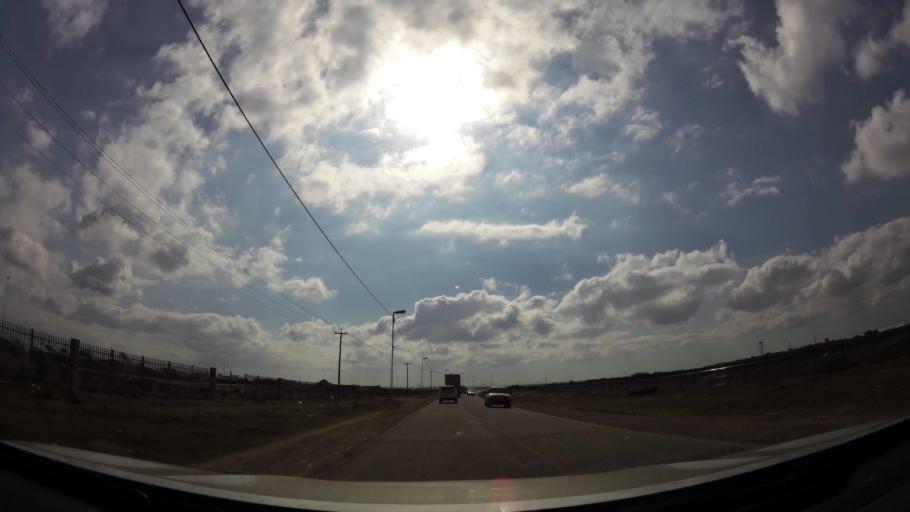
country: ZA
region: Eastern Cape
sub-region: Nelson Mandela Bay Metropolitan Municipality
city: Port Elizabeth
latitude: -33.7824
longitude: 25.5912
